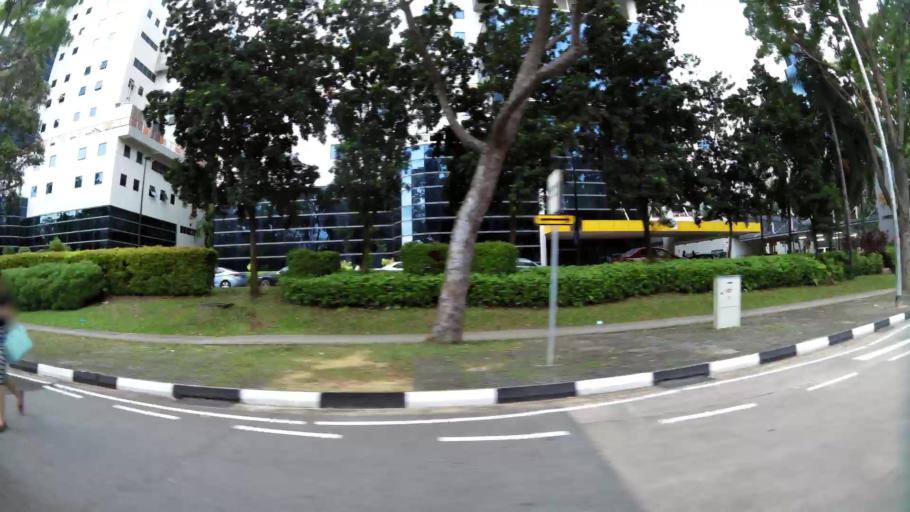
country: MY
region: Johor
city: Johor Bahru
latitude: 1.4543
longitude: 103.8098
